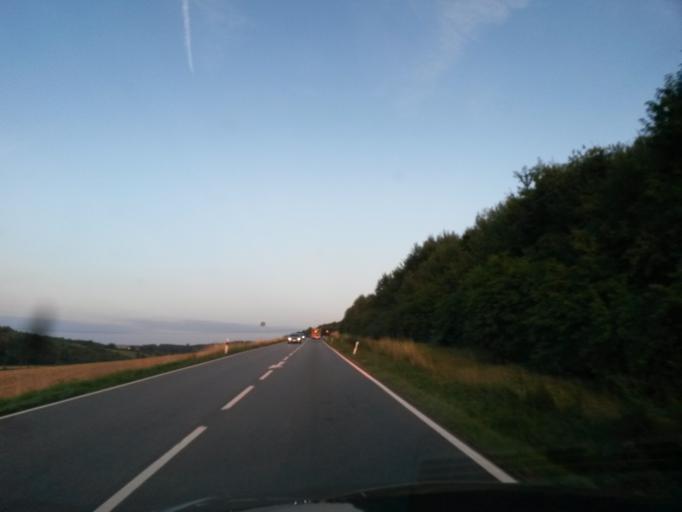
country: DE
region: Bavaria
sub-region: Regierungsbezirk Unterfranken
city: Marktheidenfeld
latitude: 49.8138
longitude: 9.6382
